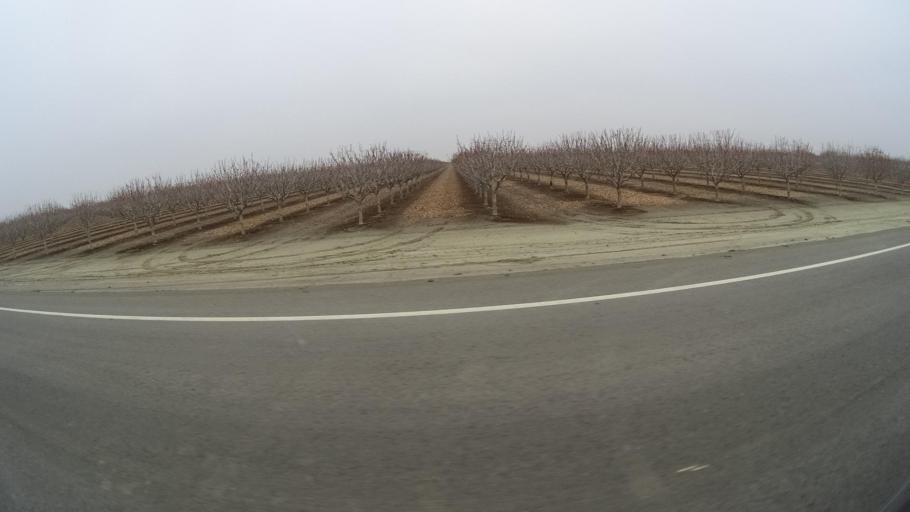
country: US
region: California
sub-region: Kern County
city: Buttonwillow
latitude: 35.3692
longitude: -119.4589
